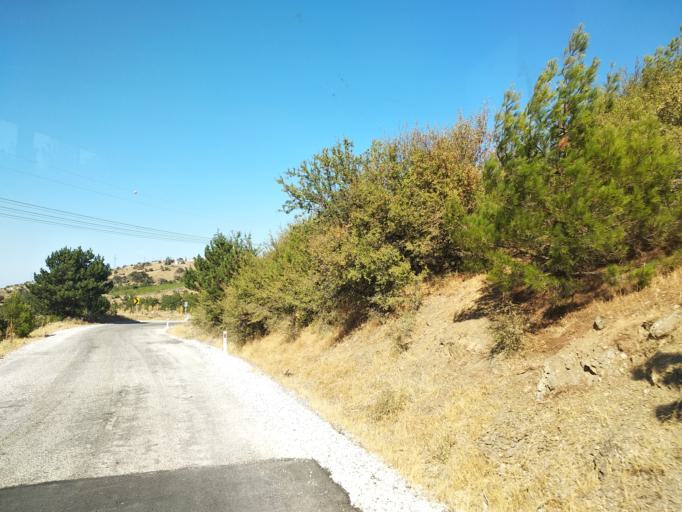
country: TR
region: Izmir
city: Gaziemir
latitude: 38.3119
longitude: 27.0005
